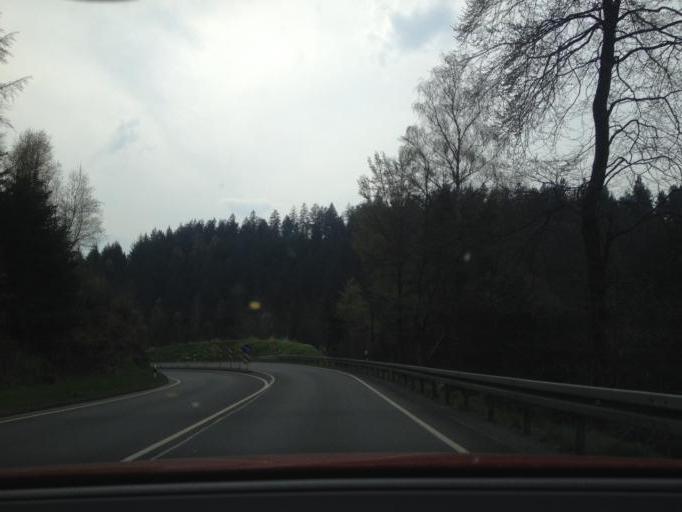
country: DE
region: Bavaria
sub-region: Upper Franconia
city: Bischofsgrun
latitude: 50.0460
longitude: 11.7436
